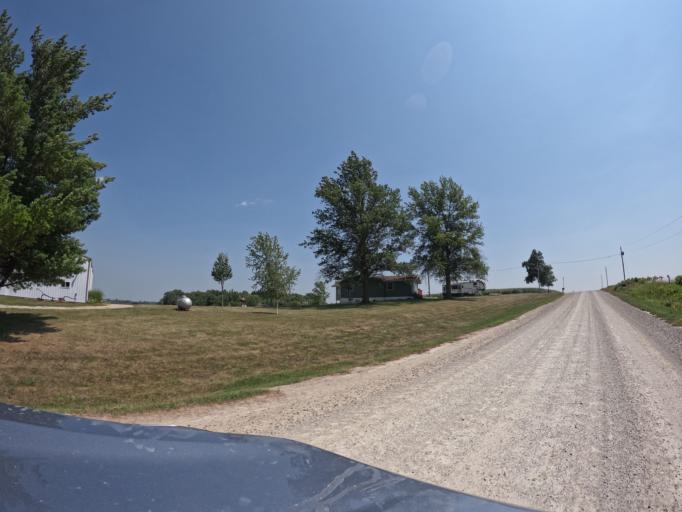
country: US
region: Iowa
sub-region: Keokuk County
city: Sigourney
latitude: 41.3446
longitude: -92.2388
